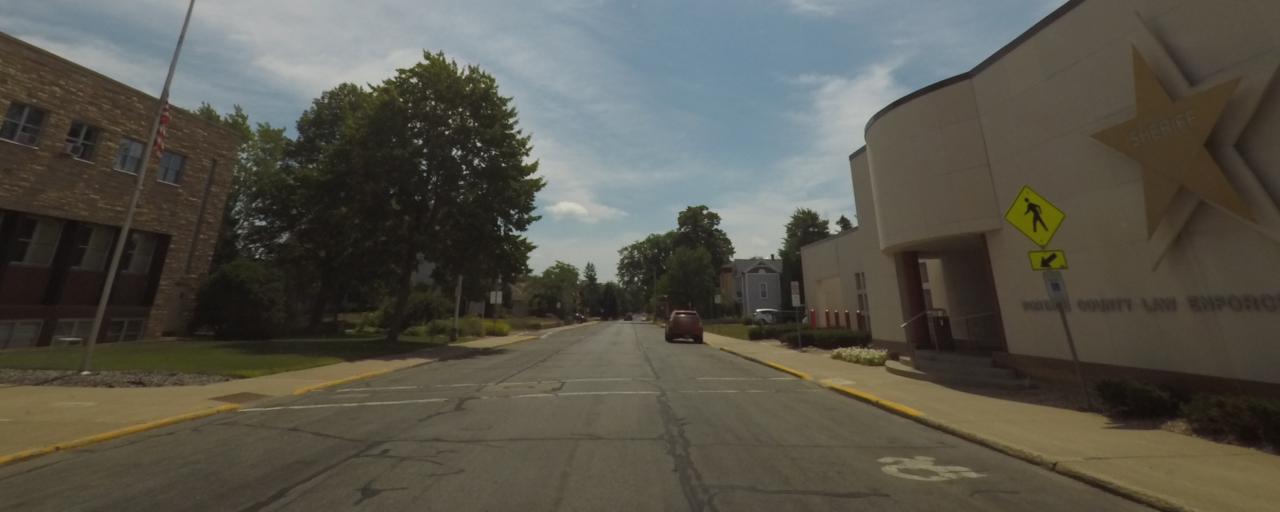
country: US
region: Wisconsin
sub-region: Portage County
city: Stevens Point
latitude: 44.5206
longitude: -89.5812
